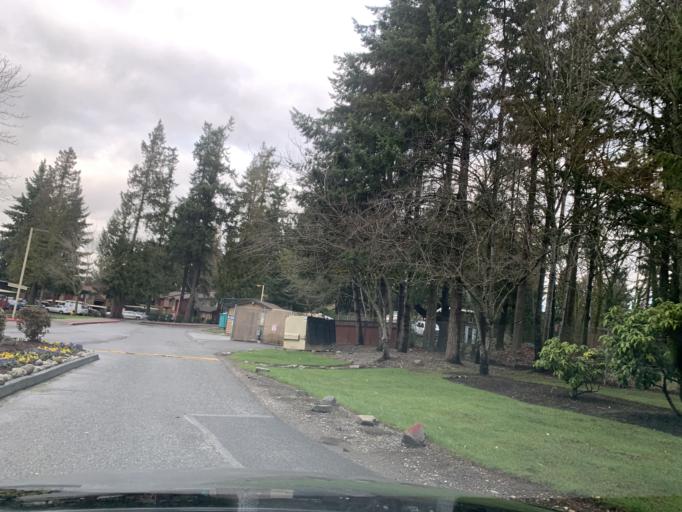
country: US
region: Washington
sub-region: Pierce County
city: Edgewood
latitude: 47.2428
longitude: -122.3006
